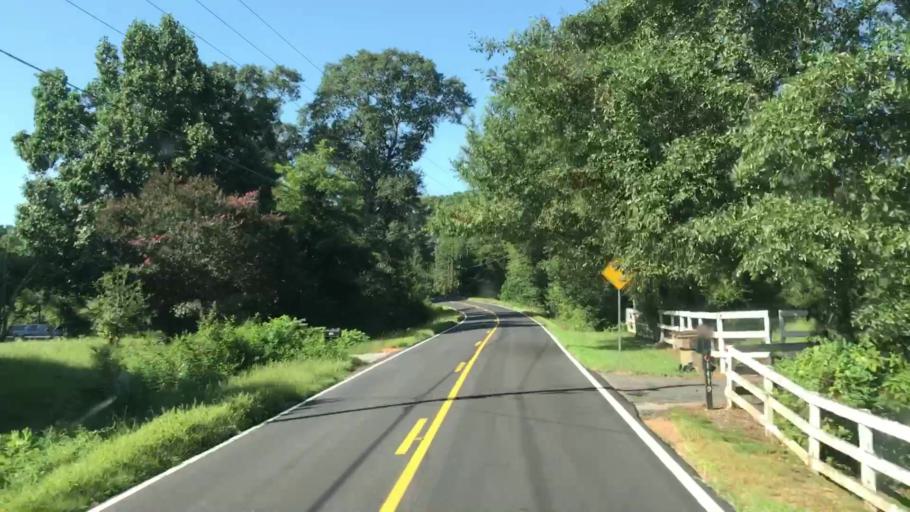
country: US
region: Georgia
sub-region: Walton County
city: Monroe
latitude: 33.8319
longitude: -83.7962
